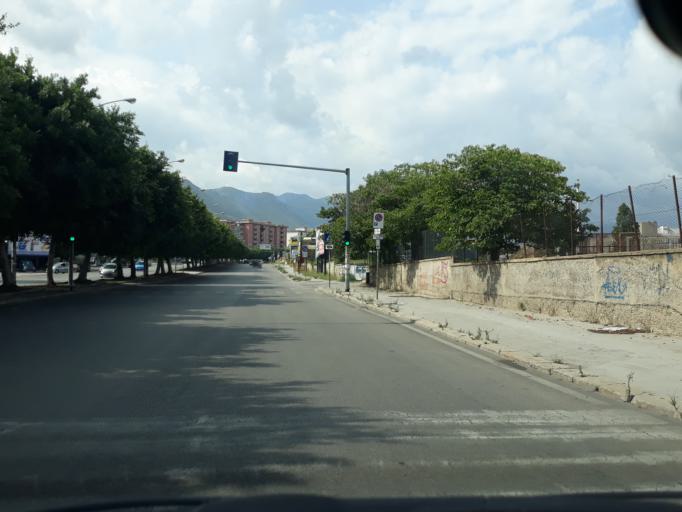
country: IT
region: Sicily
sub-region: Palermo
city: Palermo
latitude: 38.1012
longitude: 13.3476
